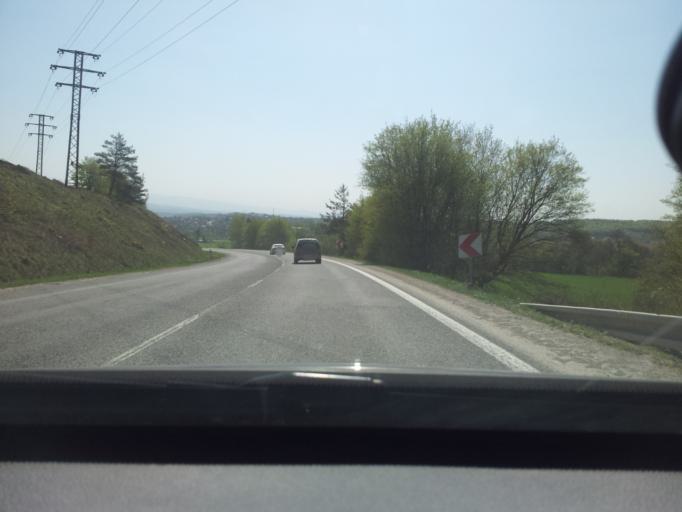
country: SK
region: Trenciansky
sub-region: Okres Trencin
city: Trencin
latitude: 48.8091
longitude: 18.0927
